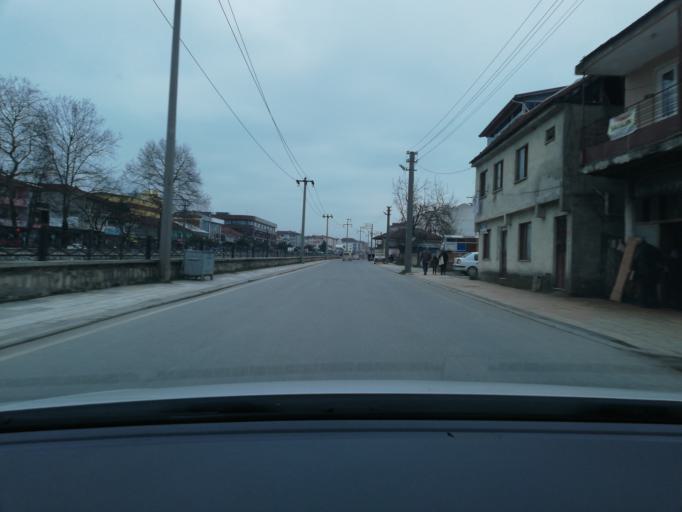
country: TR
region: Duzce
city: Duzce
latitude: 40.8374
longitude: 31.1555
